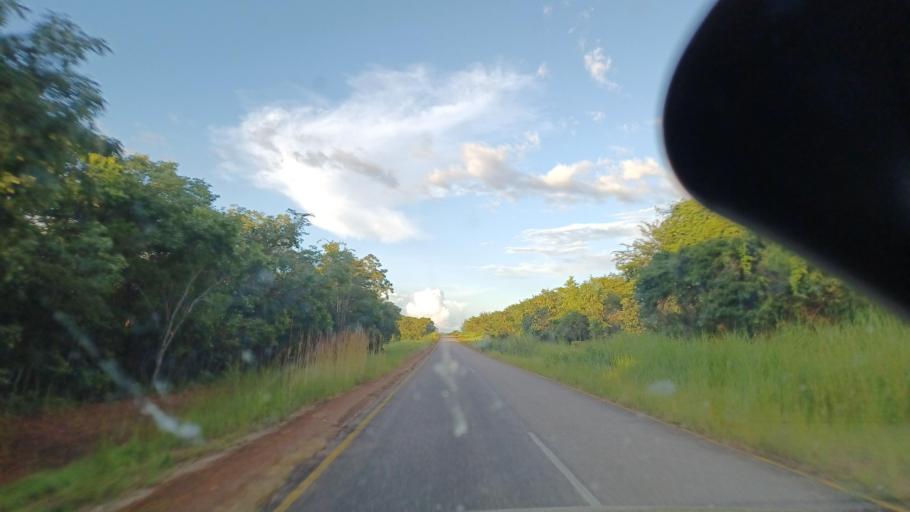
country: ZM
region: North-Western
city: Kalengwa
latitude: -13.0929
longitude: 25.2462
